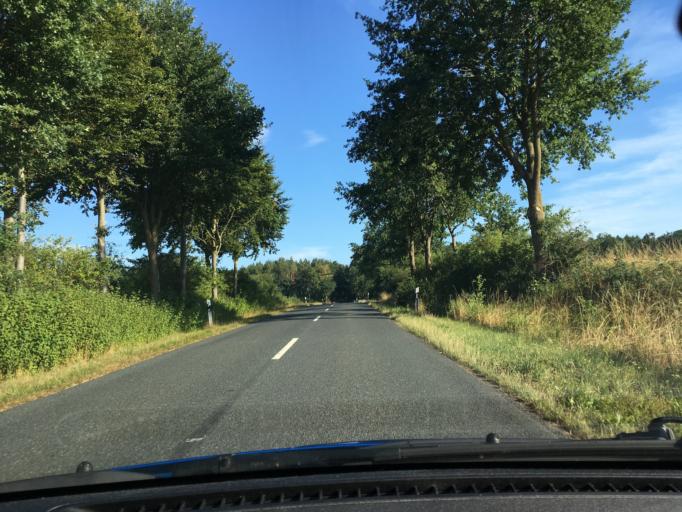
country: DE
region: Lower Saxony
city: Dahlenburg
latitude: 53.2107
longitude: 10.7053
